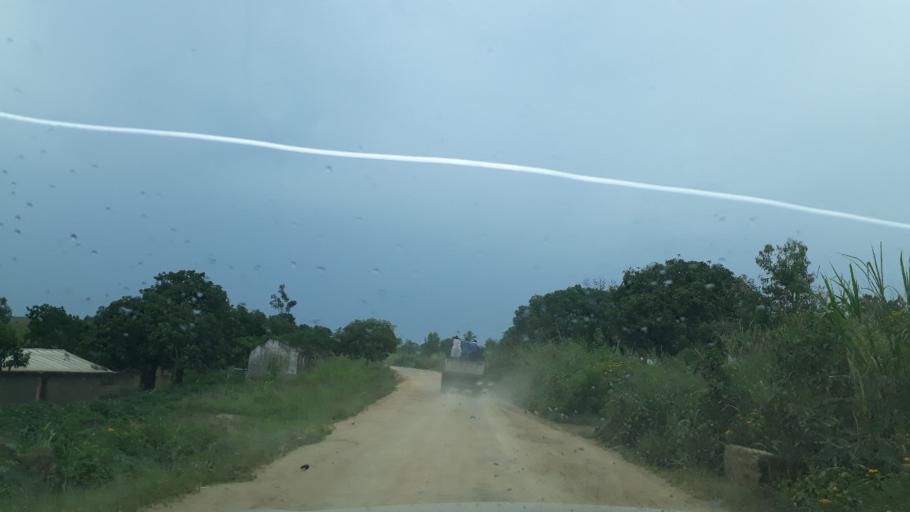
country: CD
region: Eastern Province
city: Bunia
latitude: 1.4957
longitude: 30.1668
